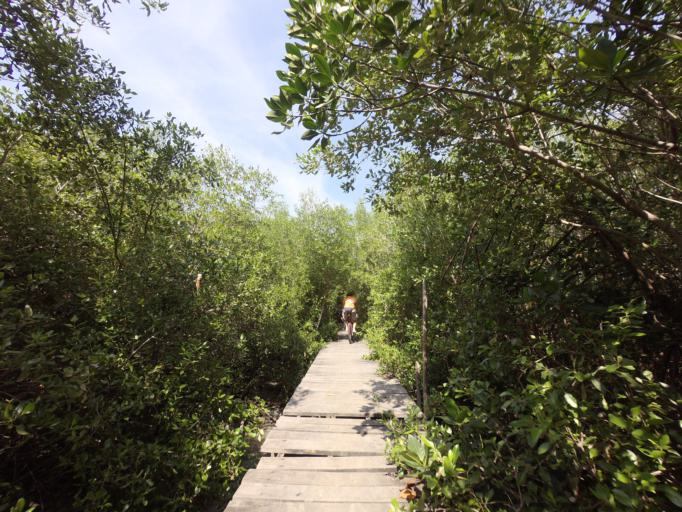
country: TH
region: Bangkok
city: Thung Khru
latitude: 13.4982
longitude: 100.4240
